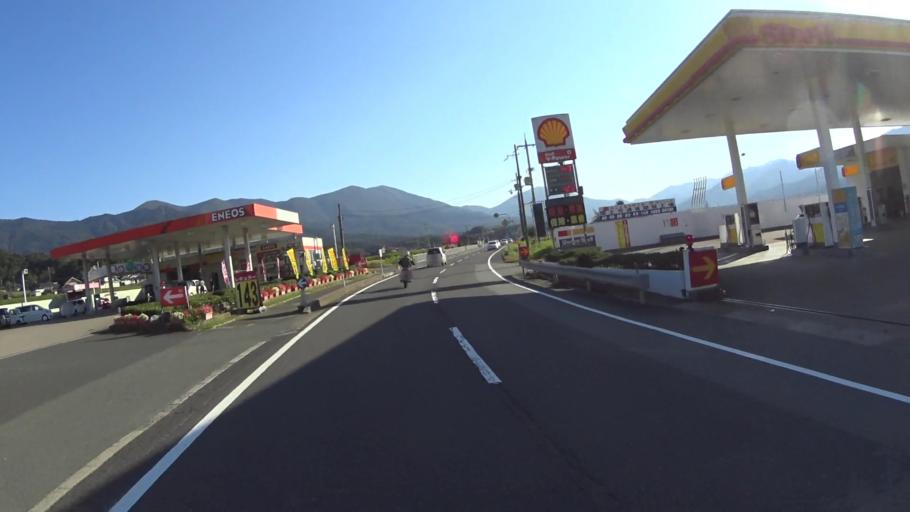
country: JP
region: Kyoto
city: Miyazu
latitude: 35.5054
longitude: 135.1039
